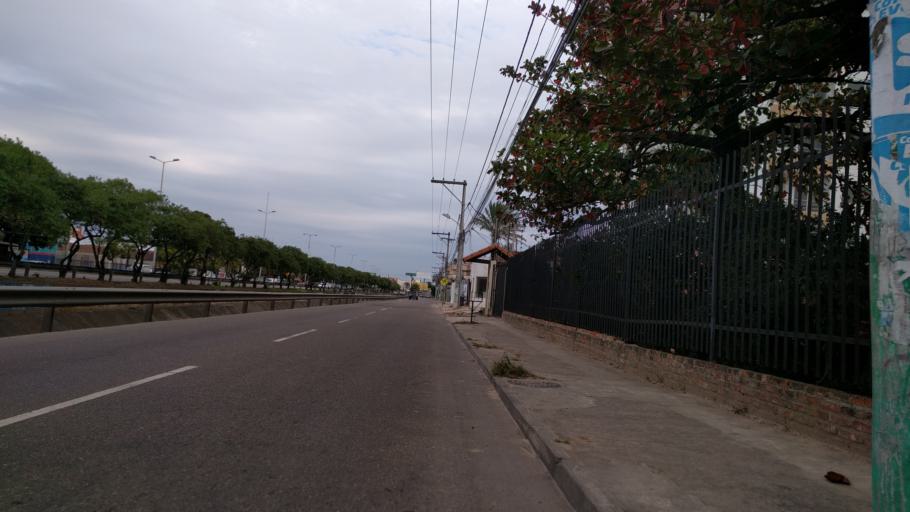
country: BO
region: Santa Cruz
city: Santa Cruz de la Sierra
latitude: -17.7805
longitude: -63.1945
